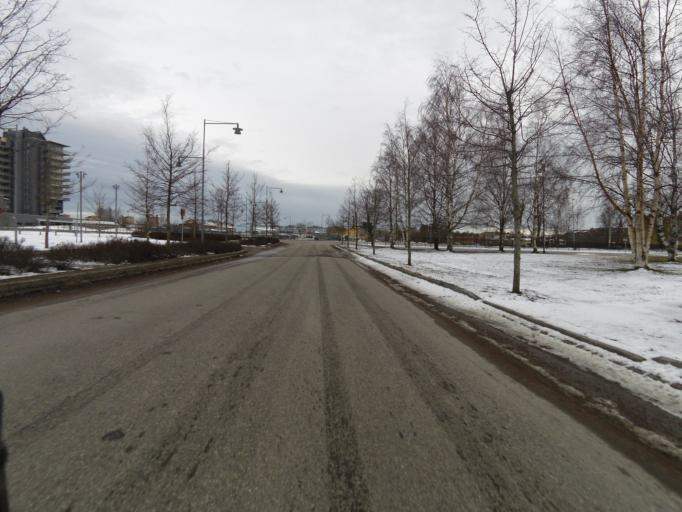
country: SE
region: Gaevleborg
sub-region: Gavle Kommun
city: Gavle
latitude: 60.6792
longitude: 17.1597
